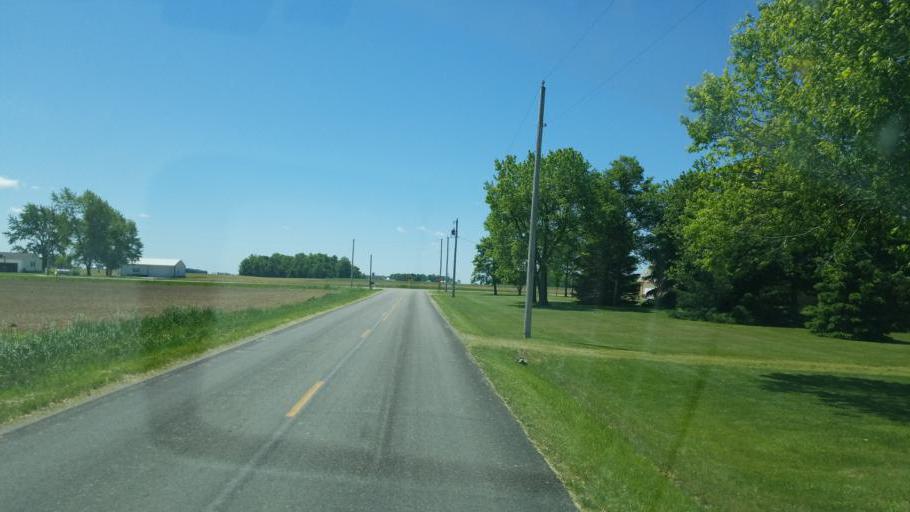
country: US
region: Ohio
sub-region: Shelby County
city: Fort Loramie
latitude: 40.3597
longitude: -84.2974
